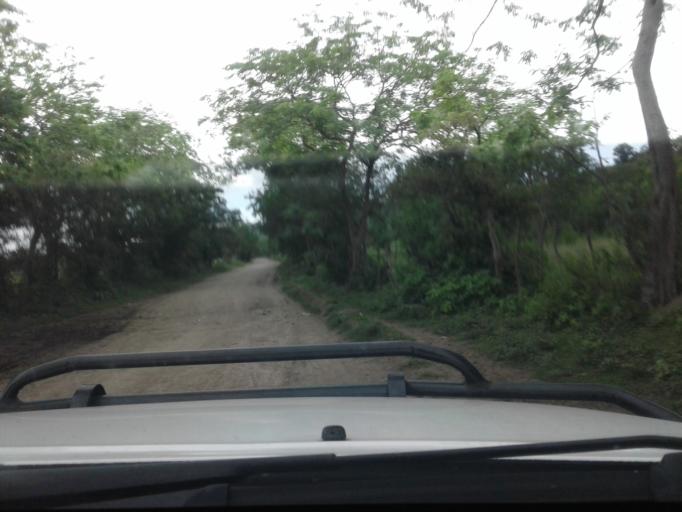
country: NI
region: Matagalpa
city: Ciudad Dario
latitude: 12.9069
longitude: -86.2015
